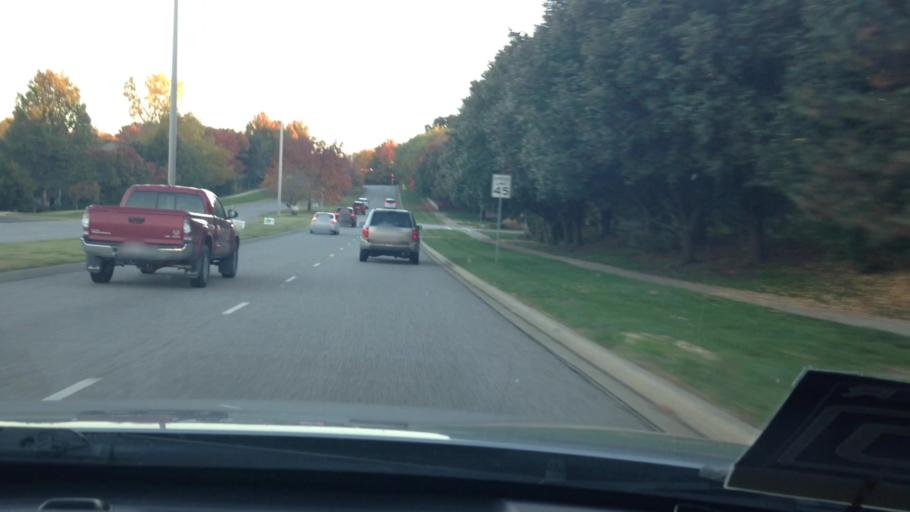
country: US
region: Kansas
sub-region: Johnson County
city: Lenexa
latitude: 38.8979
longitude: -94.7053
